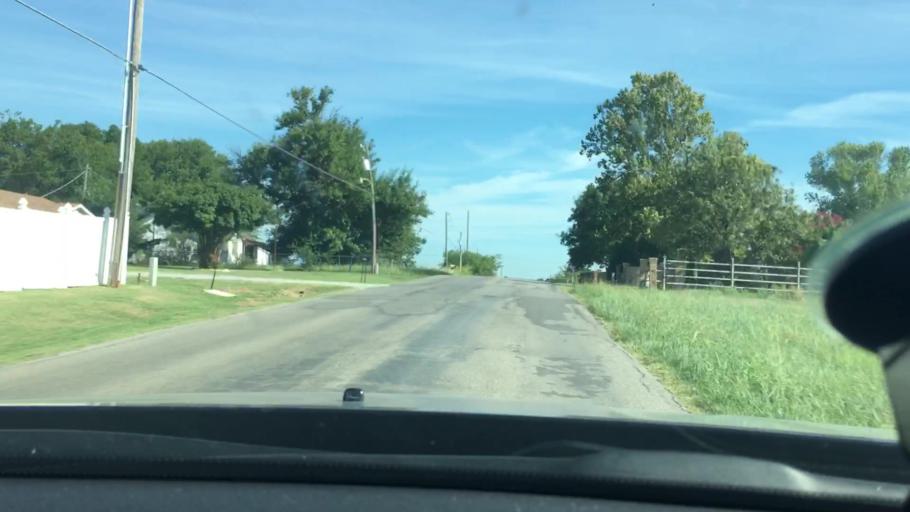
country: US
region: Oklahoma
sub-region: Carter County
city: Lone Grove
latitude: 34.1850
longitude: -97.2475
